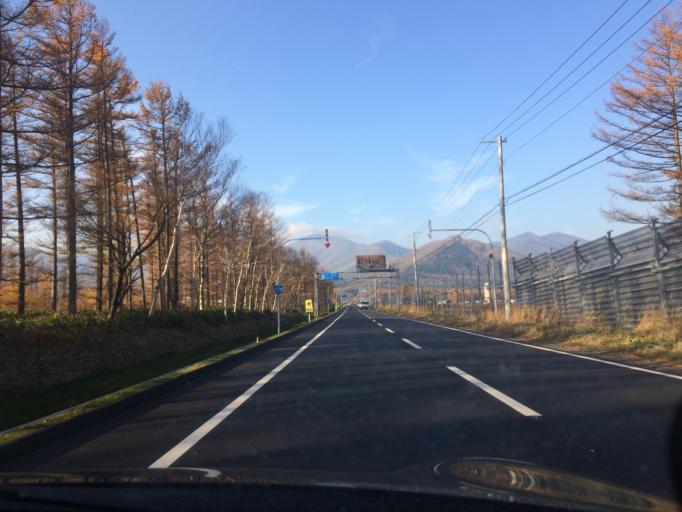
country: JP
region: Hokkaido
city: Otofuke
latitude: 42.9780
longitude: 142.8268
